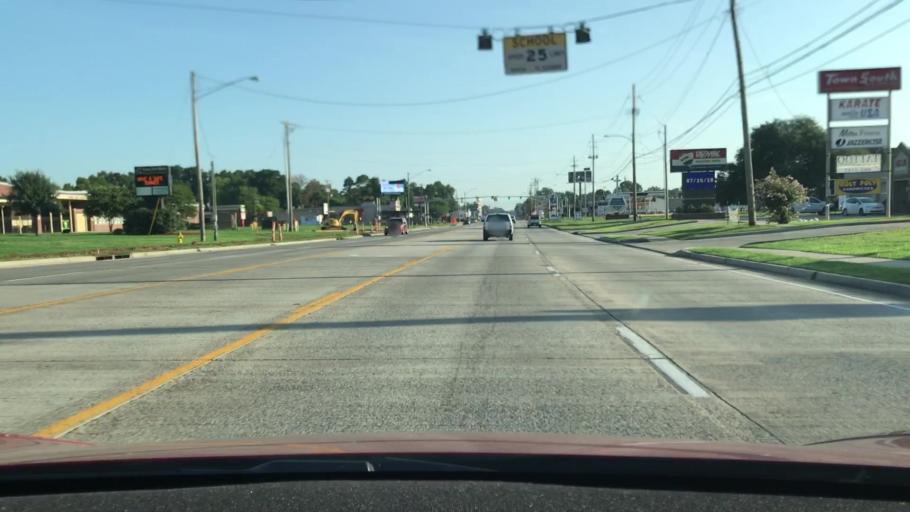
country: US
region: Louisiana
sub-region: Bossier Parish
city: Bossier City
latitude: 32.4513
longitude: -93.7221
